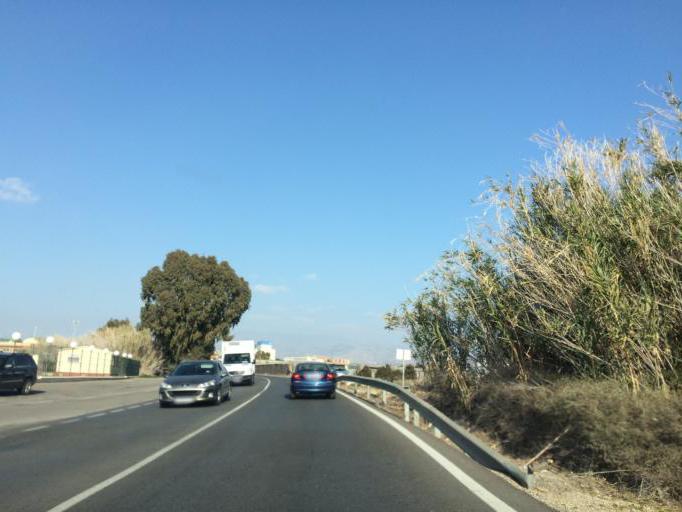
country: ES
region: Andalusia
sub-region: Provincia de Almeria
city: Almeria
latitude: 36.8482
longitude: -2.4212
